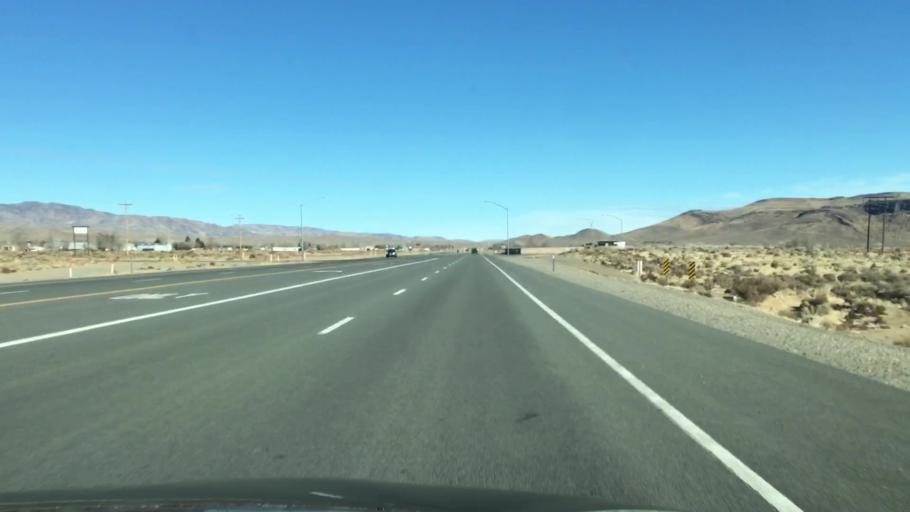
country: US
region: Nevada
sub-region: Lyon County
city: Dayton
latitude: 39.3021
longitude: -119.5168
